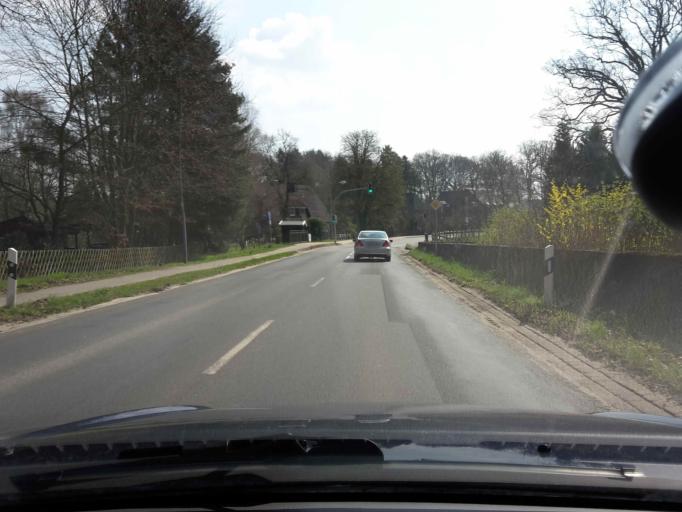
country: DE
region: Lower Saxony
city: Buchholz in der Nordheide
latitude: 53.3146
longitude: 9.9061
